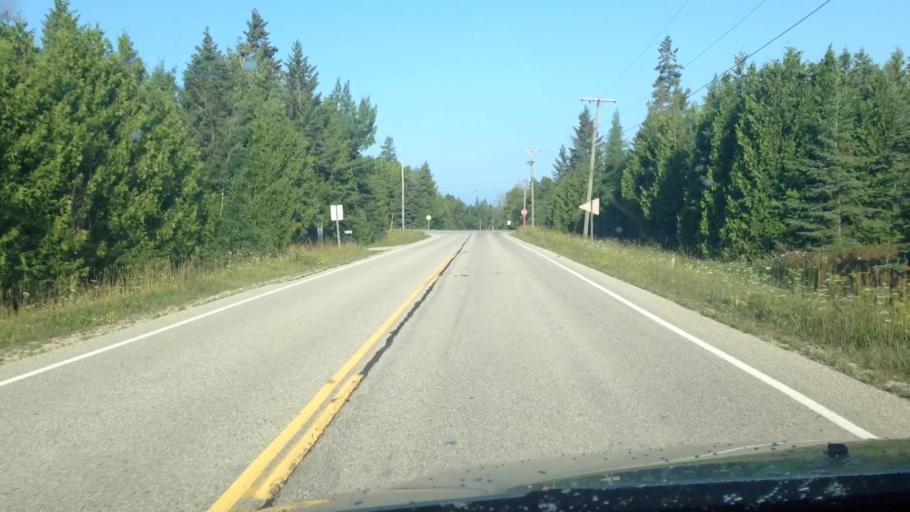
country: US
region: Michigan
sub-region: Mackinac County
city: Saint Ignace
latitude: 45.8922
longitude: -84.8307
